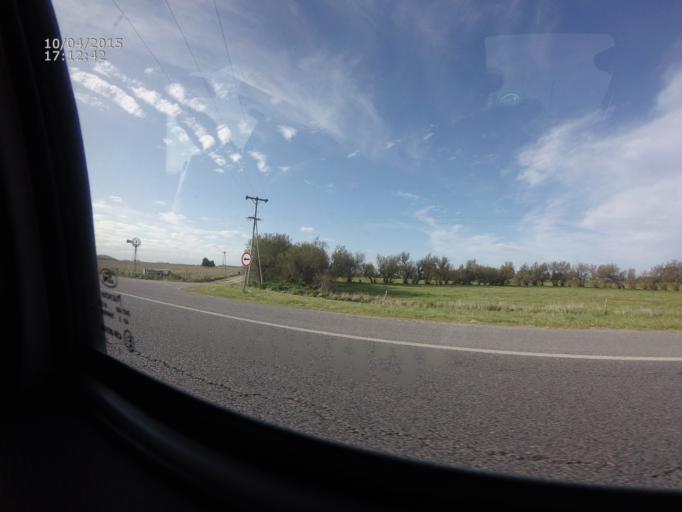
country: AR
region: Buenos Aires
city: Coronel Vidal
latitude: -37.2687
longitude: -57.7715
